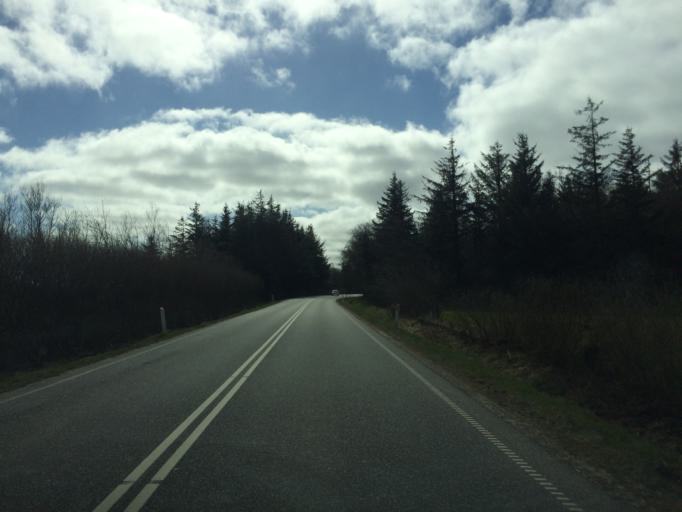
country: DK
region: Central Jutland
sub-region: Holstebro Kommune
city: Ulfborg
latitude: 56.2984
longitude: 8.1887
